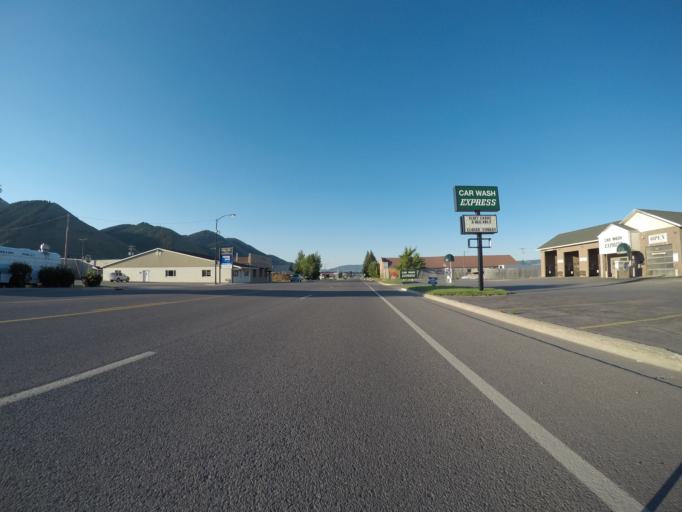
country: US
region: Wyoming
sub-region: Lincoln County
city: Afton
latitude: 42.7215
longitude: -110.9337
